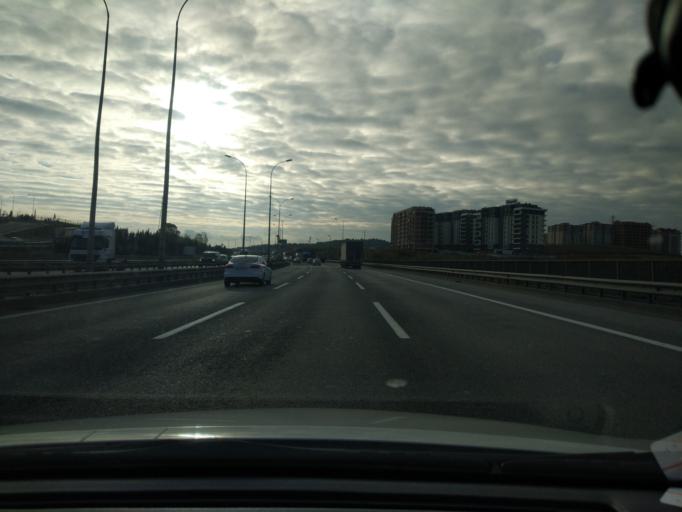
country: TR
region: Kocaeli
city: Balcik
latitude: 40.8402
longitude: 29.4154
